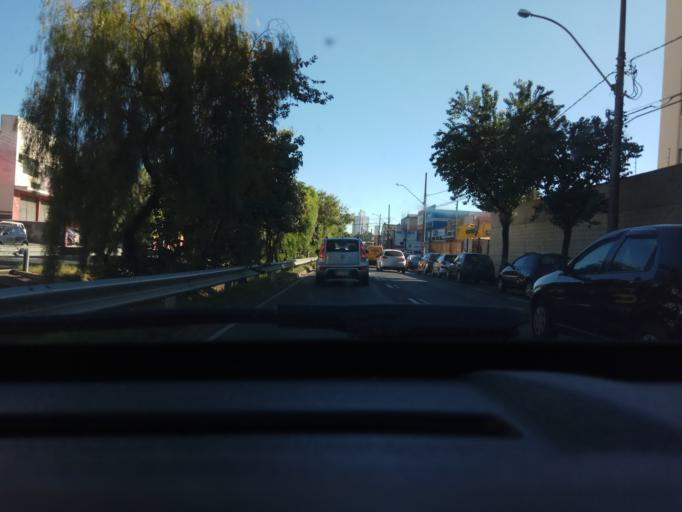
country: BR
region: Sao Paulo
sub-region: Piracicaba
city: Piracicaba
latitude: -22.7434
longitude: -47.6451
